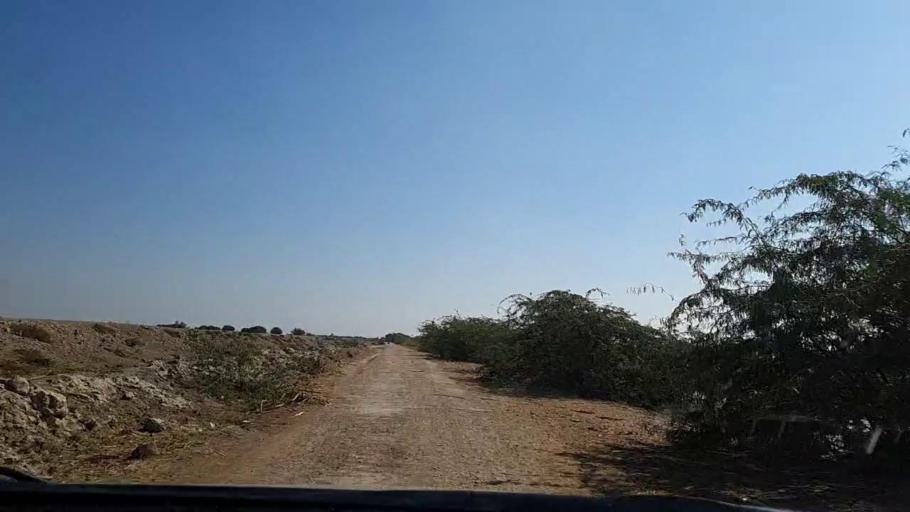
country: PK
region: Sindh
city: Tando Mittha Khan
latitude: 25.7702
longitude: 69.2964
